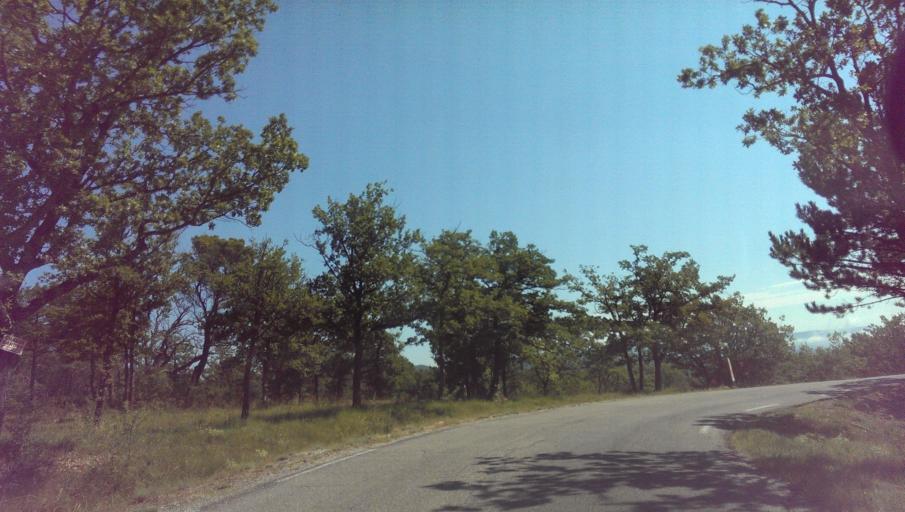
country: FR
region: Provence-Alpes-Cote d'Azur
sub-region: Departement du Vaucluse
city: Gordes
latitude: 43.9551
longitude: 5.2061
